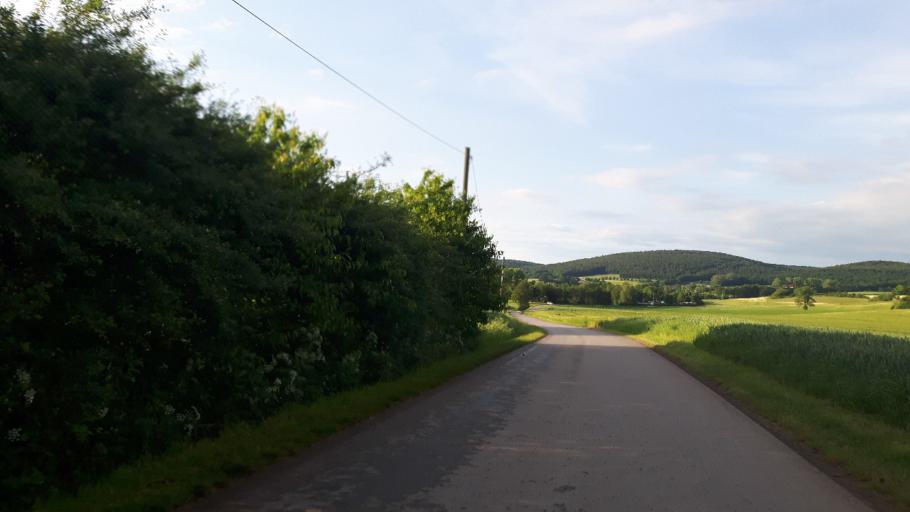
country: DE
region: Bavaria
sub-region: Regierungsbezirk Unterfranken
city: Sulzfeld
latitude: 50.2457
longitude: 10.4044
